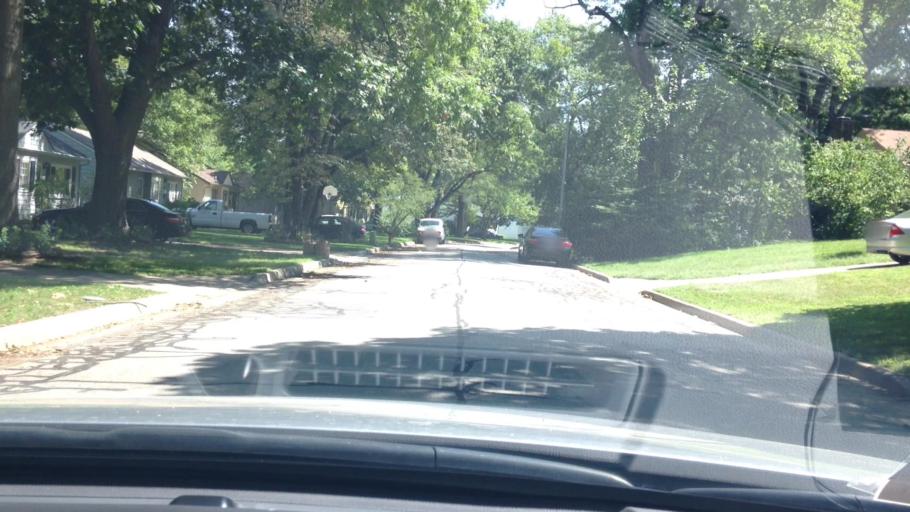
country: US
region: Kansas
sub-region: Johnson County
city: Roeland Park
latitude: 39.0324
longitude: -94.6420
